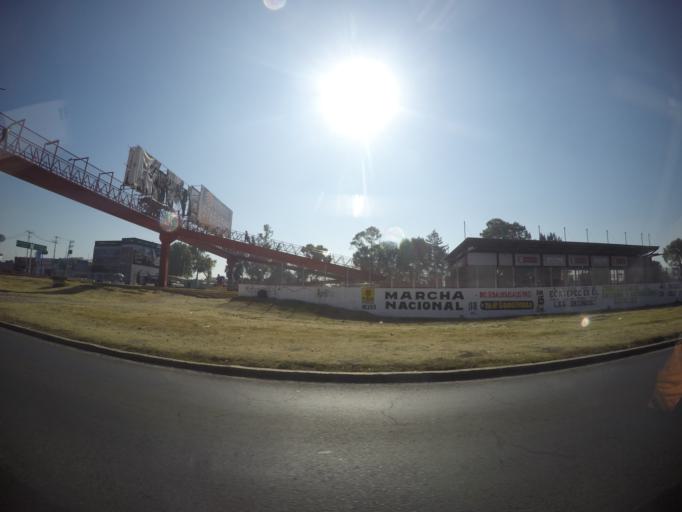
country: MX
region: Mexico
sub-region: Atenco
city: Colonia el Salado
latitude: 19.6015
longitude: -99.0161
